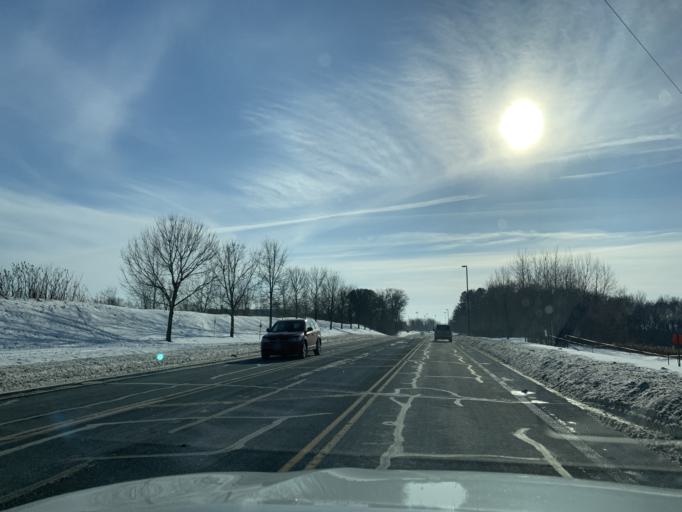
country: US
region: Minnesota
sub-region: Anoka County
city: Columbus
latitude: 45.2491
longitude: -93.0349
